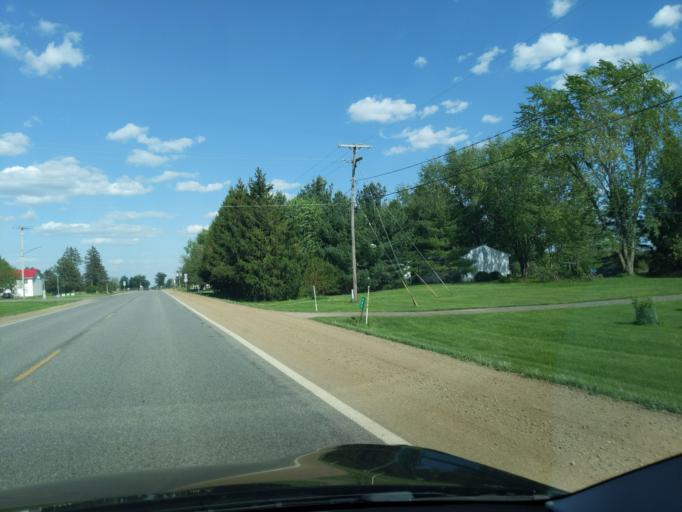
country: US
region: Michigan
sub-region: Ionia County
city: Portland
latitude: 42.7558
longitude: -84.9916
